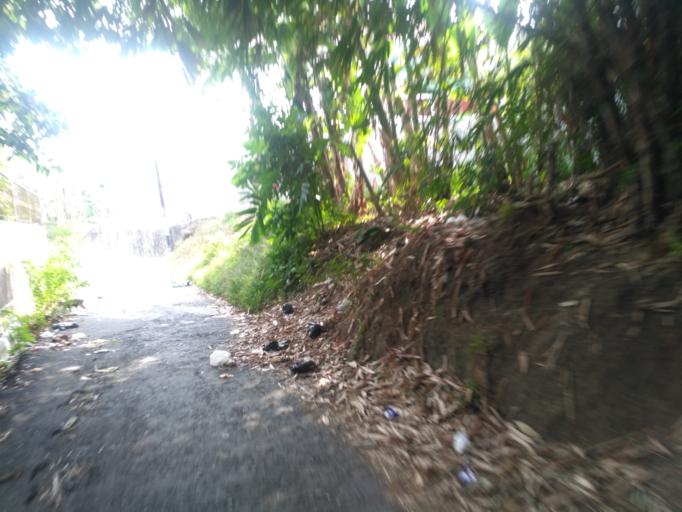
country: ID
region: Daerah Istimewa Yogyakarta
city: Melati
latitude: -7.7542
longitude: 110.3687
